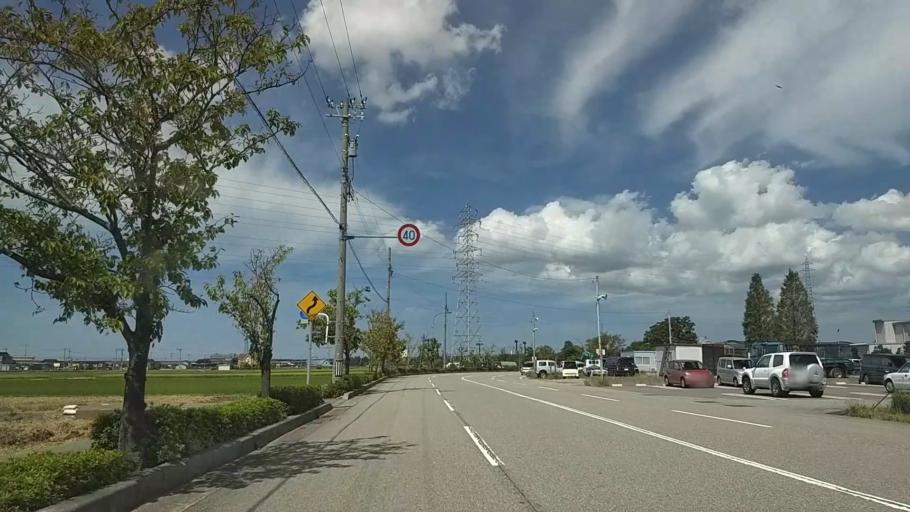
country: JP
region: Ishikawa
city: Kanazawa-shi
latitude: 36.5916
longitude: 136.6563
